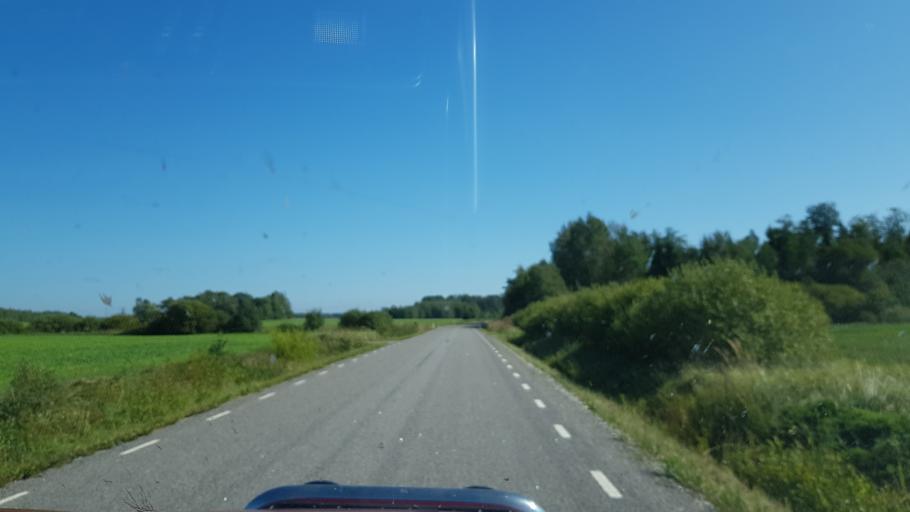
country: EE
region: Polvamaa
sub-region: Polva linn
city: Polva
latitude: 58.2176
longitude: 27.2051
